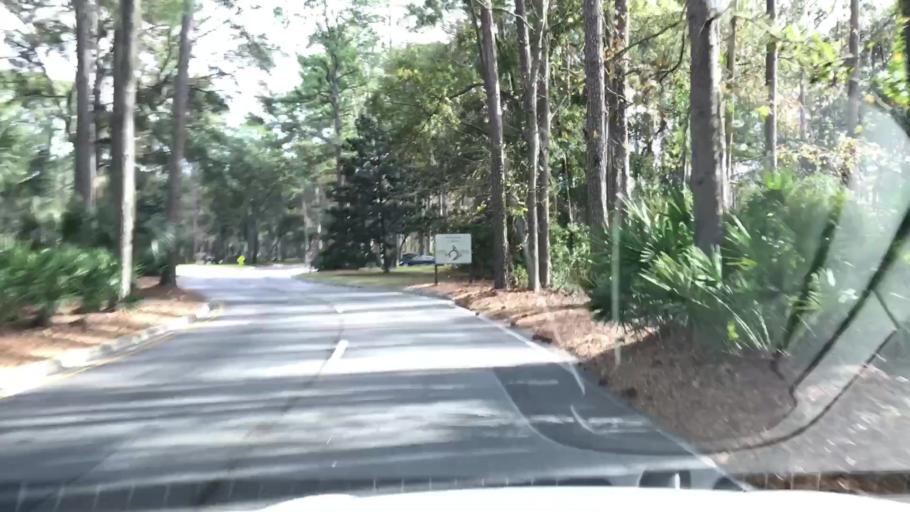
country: US
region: South Carolina
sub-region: Beaufort County
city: Hilton Head Island
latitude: 32.2169
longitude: -80.7227
